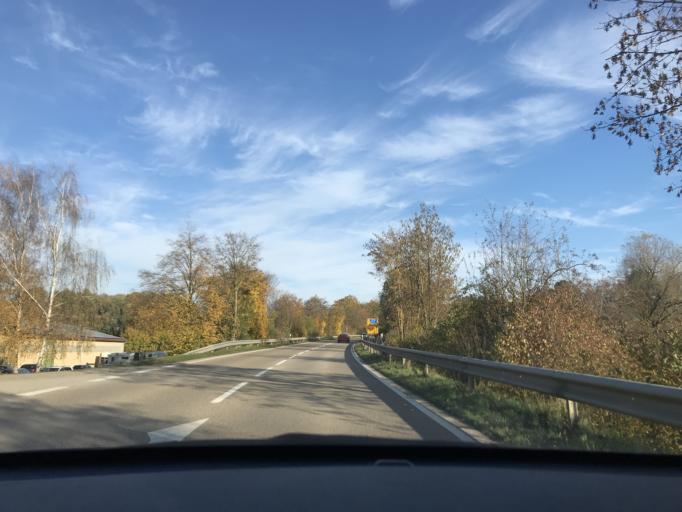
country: DE
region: Bavaria
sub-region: Lower Bavaria
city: Bad Abbach
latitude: 48.9362
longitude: 12.0777
